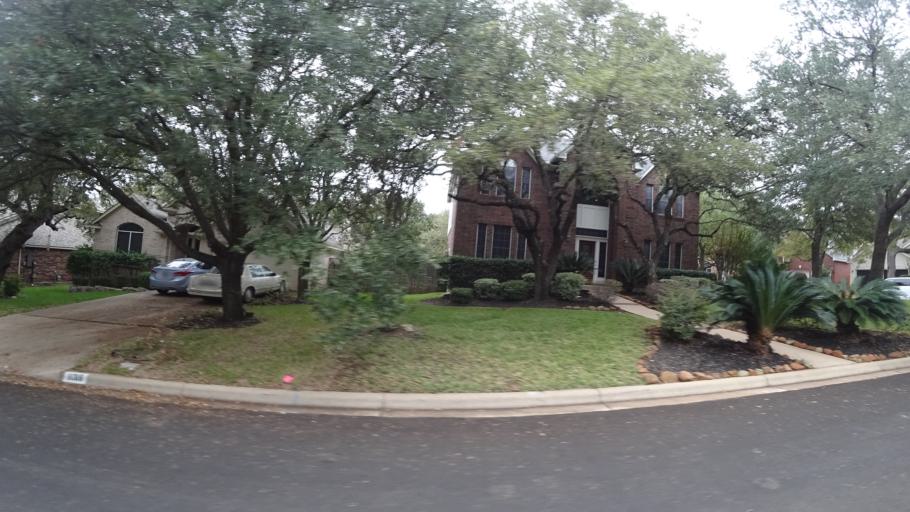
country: US
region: Texas
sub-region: Travis County
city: Shady Hollow
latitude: 30.1839
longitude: -97.8936
